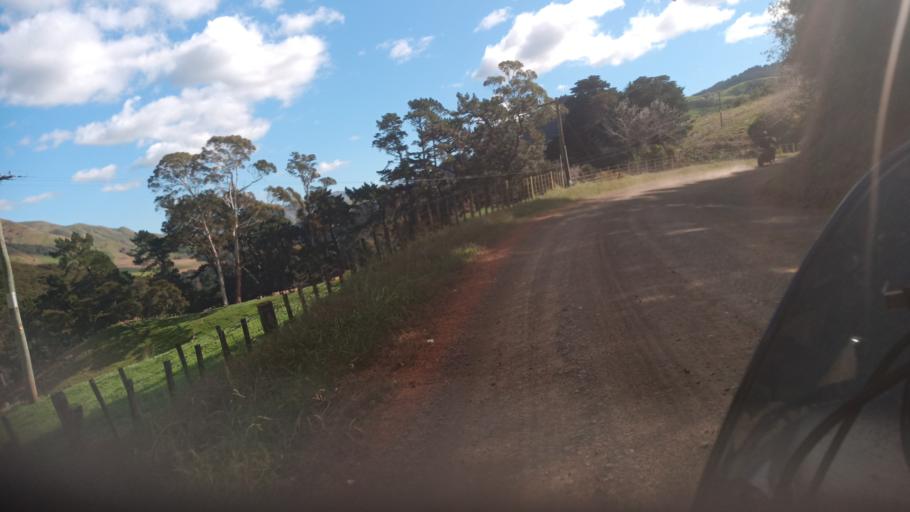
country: NZ
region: Gisborne
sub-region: Gisborne District
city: Gisborne
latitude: -38.4158
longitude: 177.6944
